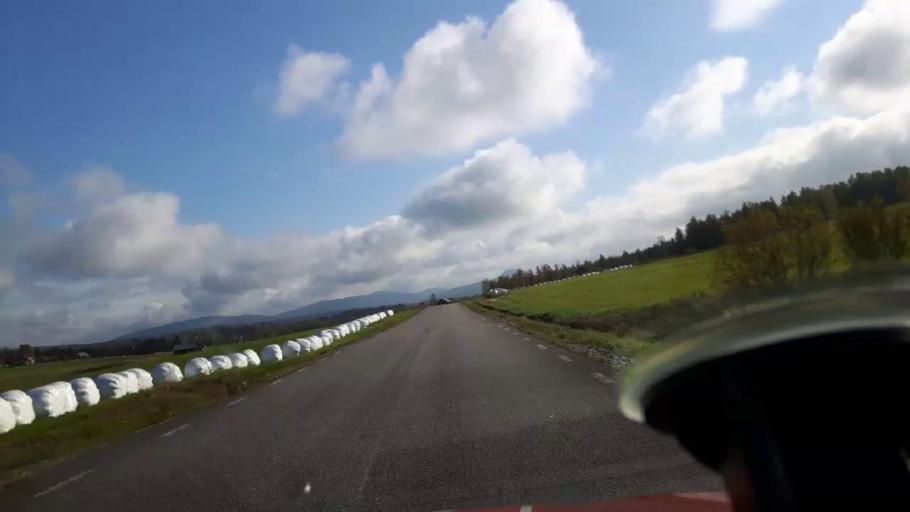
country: SE
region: Gaevleborg
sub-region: Ljusdals Kommun
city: Ljusdal
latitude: 61.7629
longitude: 16.0698
